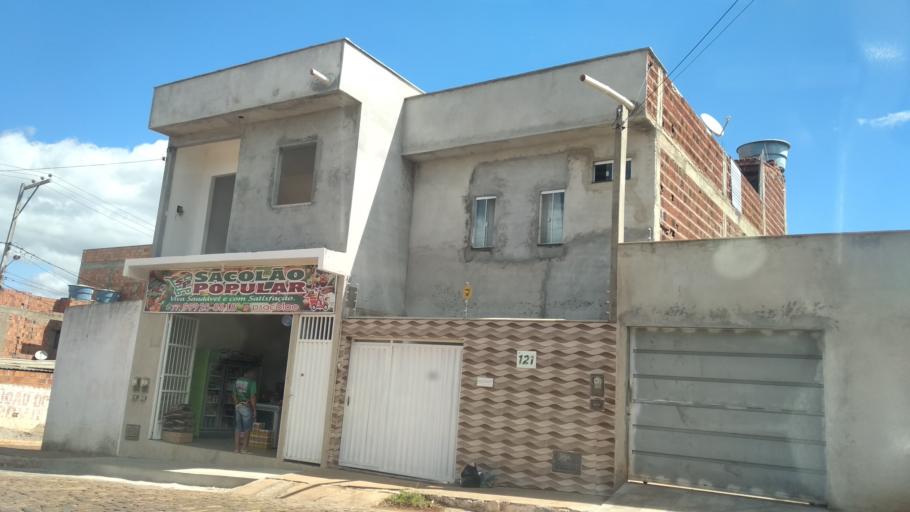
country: BR
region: Bahia
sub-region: Caetite
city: Caetite
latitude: -14.0597
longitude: -42.4855
